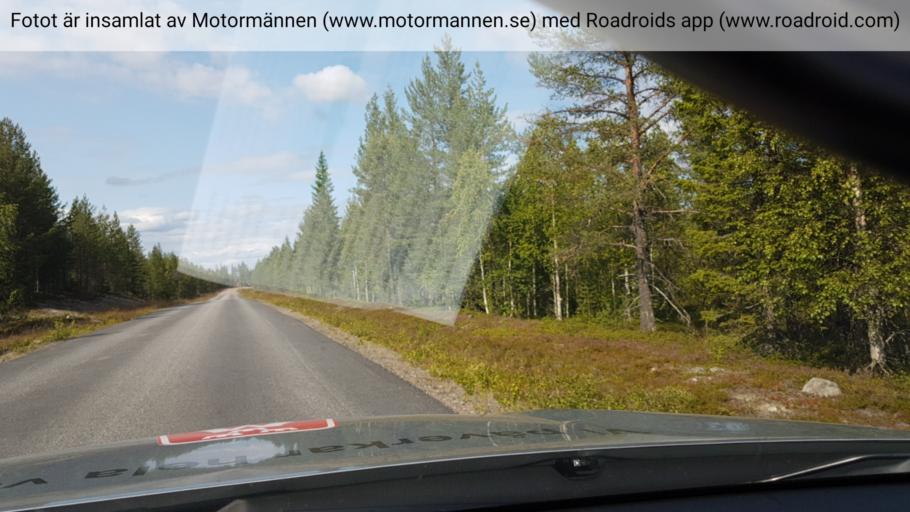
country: SE
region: Vaesterbotten
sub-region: Skelleftea Kommun
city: Storvik
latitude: 65.3511
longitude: 20.3380
